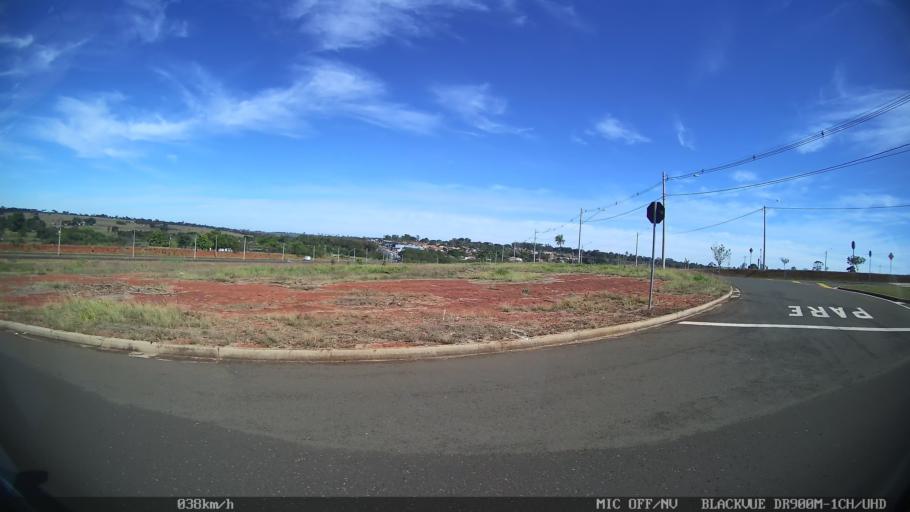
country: BR
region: Sao Paulo
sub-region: Sao Jose Do Rio Preto
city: Sao Jose do Rio Preto
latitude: -20.8553
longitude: -49.3737
